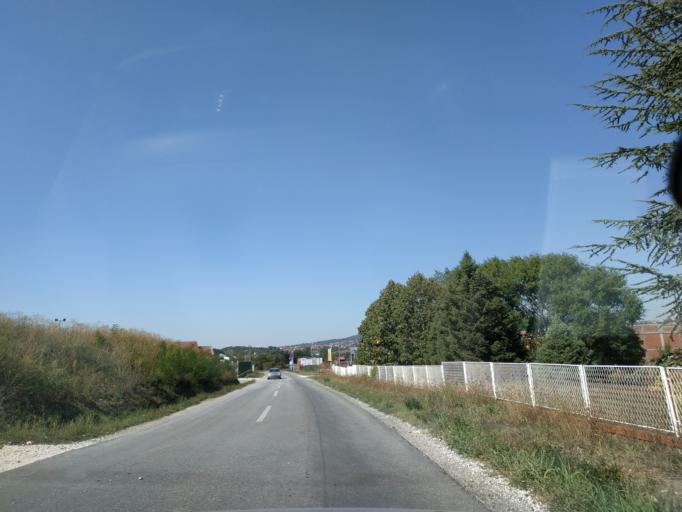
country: RS
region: Central Serbia
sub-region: Sumadijski Okrug
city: Arangelovac
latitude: 44.2923
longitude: 20.6033
